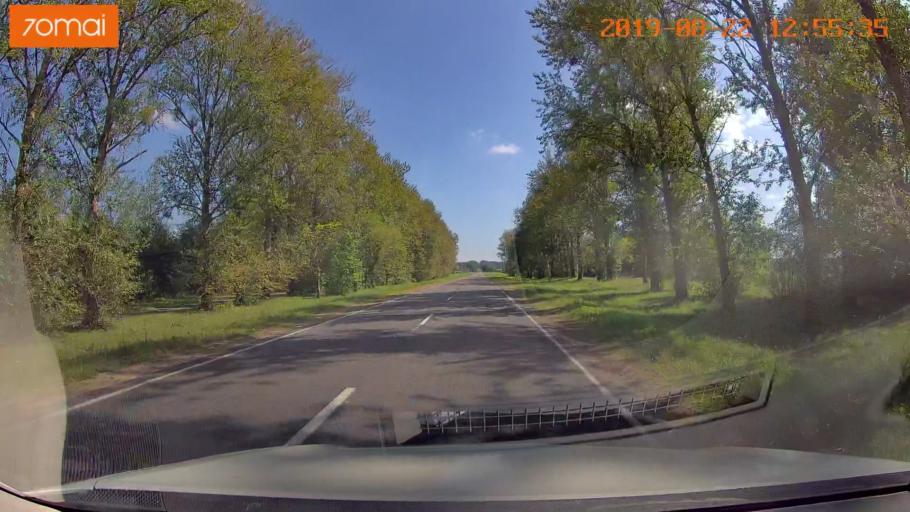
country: BY
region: Minsk
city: Prawdzinski
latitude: 53.4364
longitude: 27.7151
